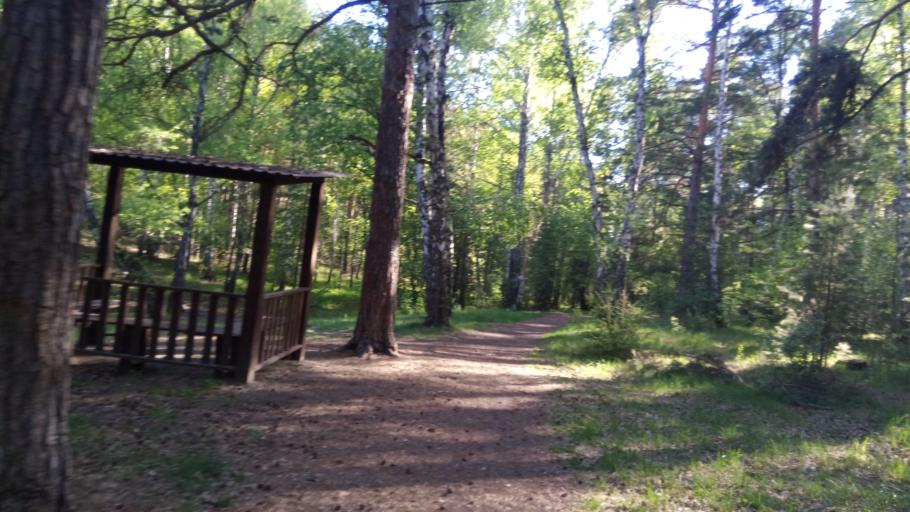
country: RU
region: Chelyabinsk
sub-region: Gorod Chelyabinsk
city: Chelyabinsk
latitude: 55.1412
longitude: 61.3388
